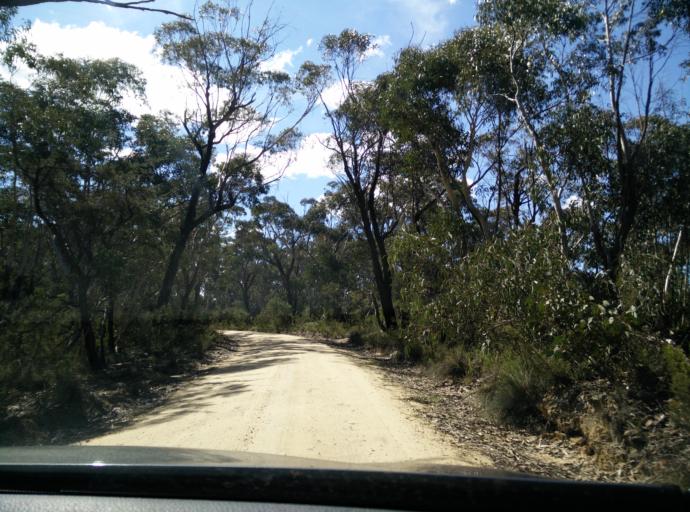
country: AU
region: New South Wales
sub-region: Blue Mountains Municipality
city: Blackheath
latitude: -33.5699
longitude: 150.2880
